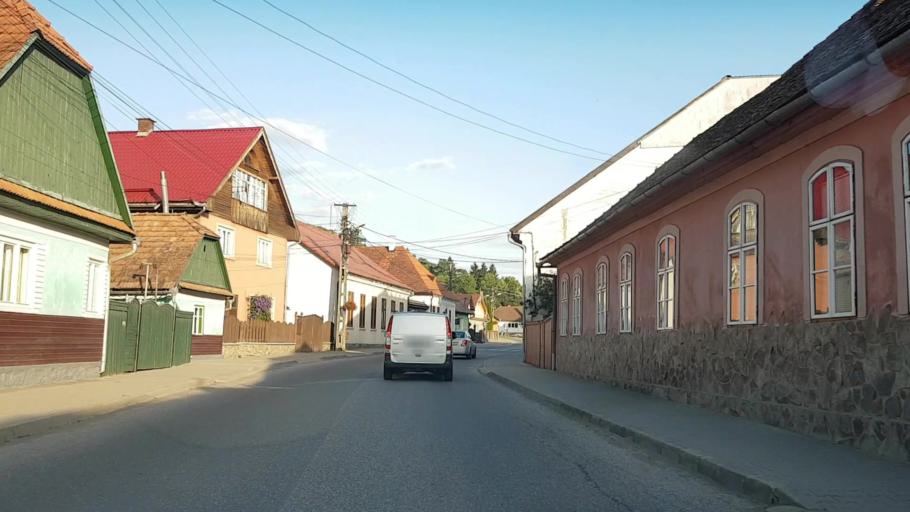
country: RO
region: Harghita
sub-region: Comuna Praid
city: Praid
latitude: 46.5520
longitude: 25.1266
